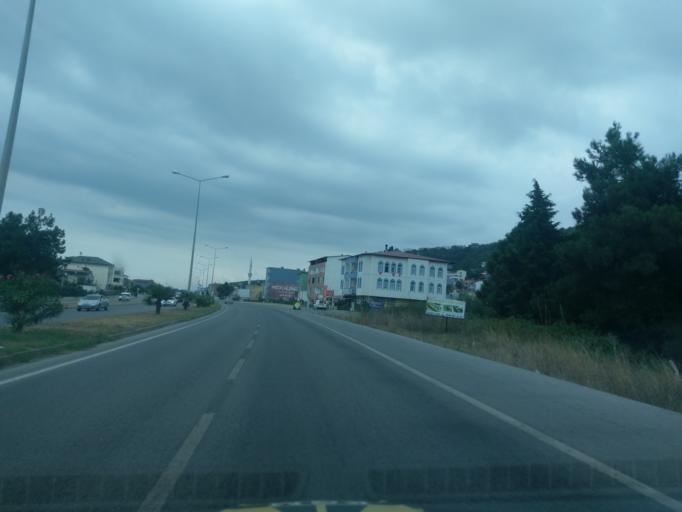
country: TR
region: Samsun
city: Taflan
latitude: 41.3886
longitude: 36.2043
